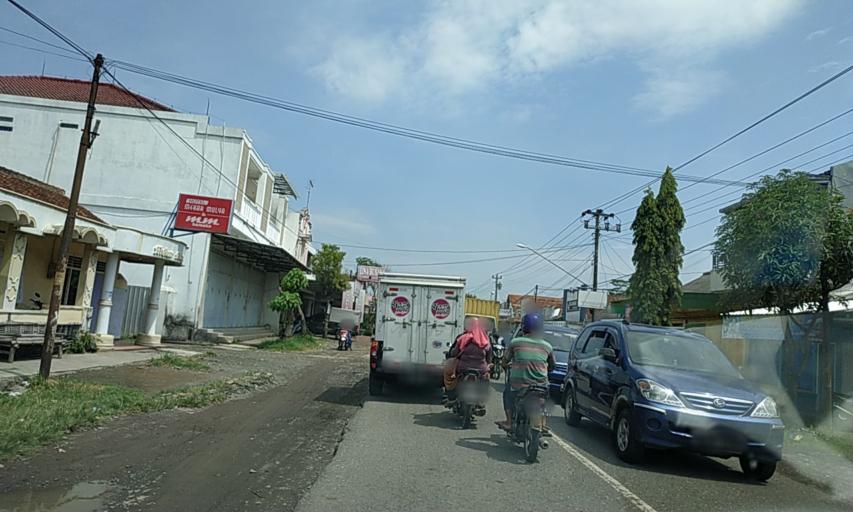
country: ID
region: Central Java
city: Sidamulya
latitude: -7.4860
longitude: 108.8059
